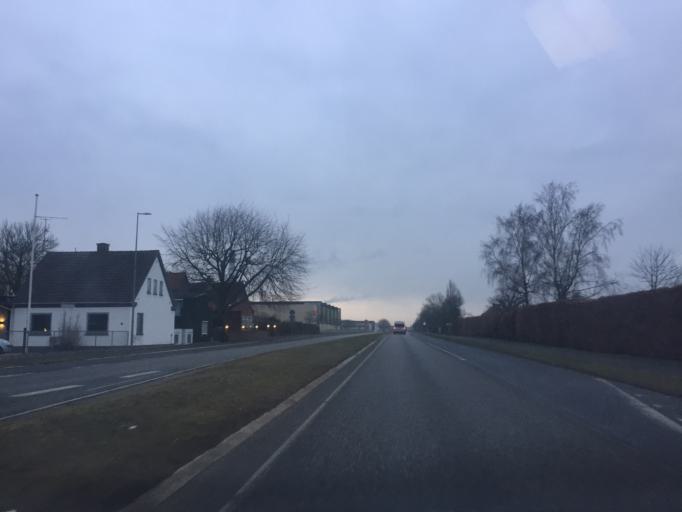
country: DK
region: Zealand
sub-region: Solrod Kommune
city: Solrod Strand
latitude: 55.5358
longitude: 12.2080
